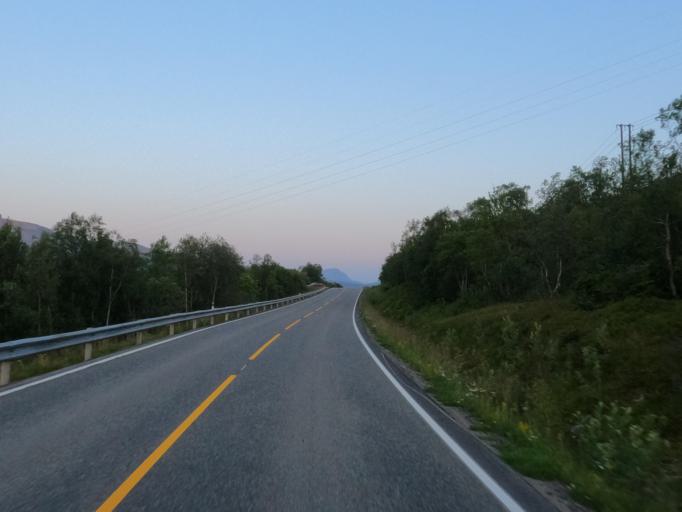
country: NO
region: Nordland
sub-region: Lodingen
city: Lodingen
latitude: 68.5188
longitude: 16.1038
